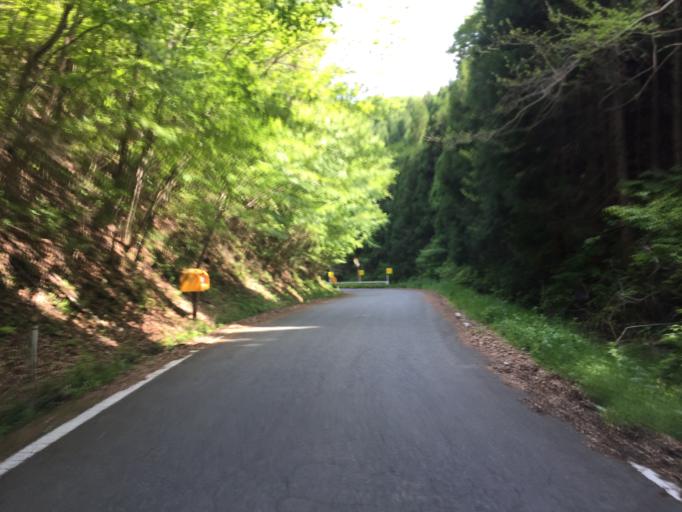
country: JP
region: Fukushima
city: Ishikawa
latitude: 37.0033
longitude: 140.5987
